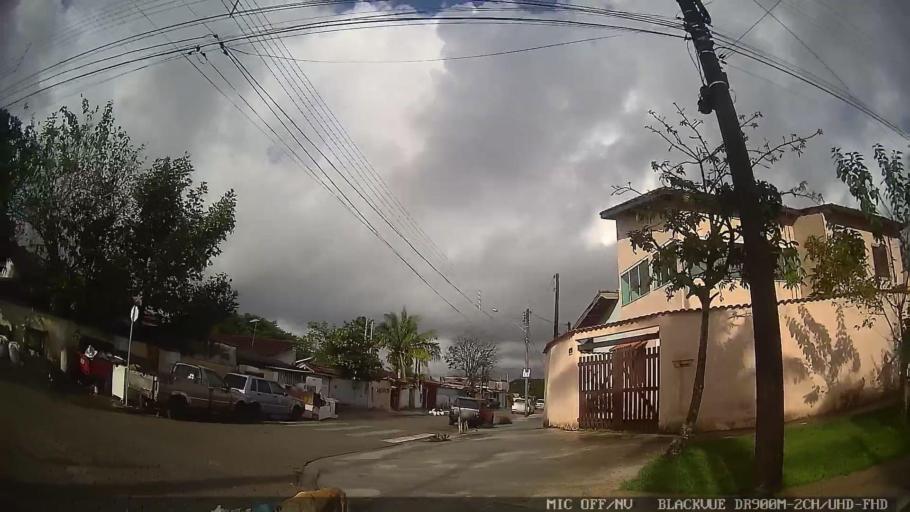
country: BR
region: Sao Paulo
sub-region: Itanhaem
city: Itanhaem
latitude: -24.2059
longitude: -46.8749
